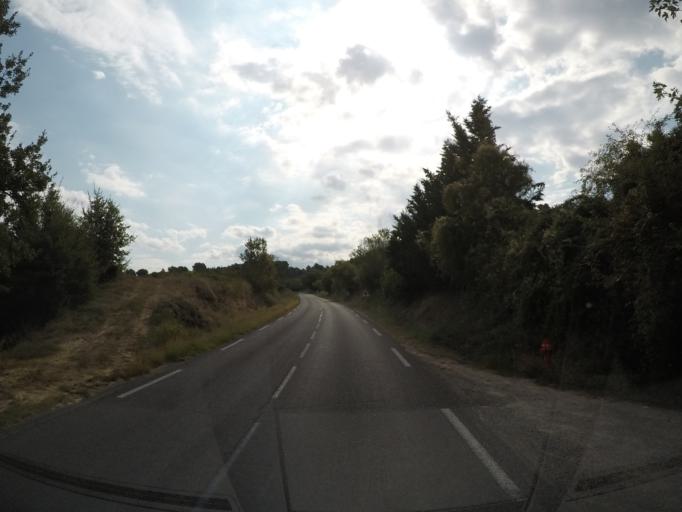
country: FR
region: Provence-Alpes-Cote d'Azur
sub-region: Departement du Vaucluse
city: Ansouis
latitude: 43.7299
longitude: 5.4888
